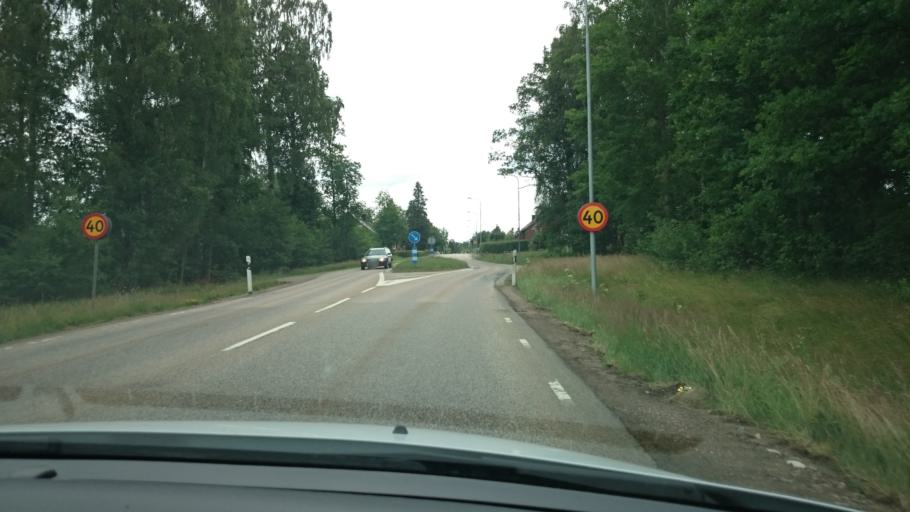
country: SE
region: Halland
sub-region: Hylte Kommun
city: Hyltebruk
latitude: 56.9907
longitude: 13.2285
